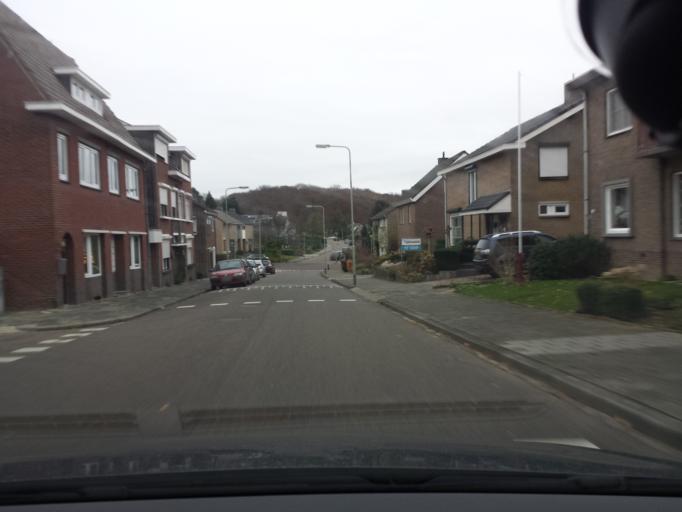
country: NL
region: Limburg
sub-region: Gemeente Heerlen
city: Heerlen
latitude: 50.8977
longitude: 6.0200
